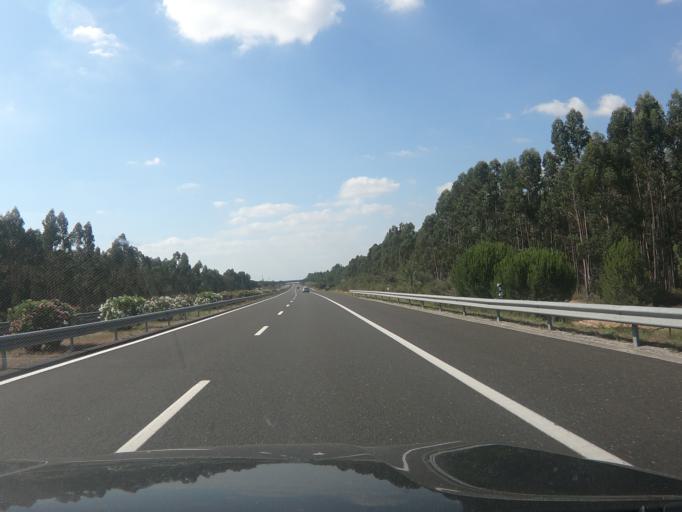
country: PT
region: Santarem
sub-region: Benavente
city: Poceirao
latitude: 38.7918
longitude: -8.6906
